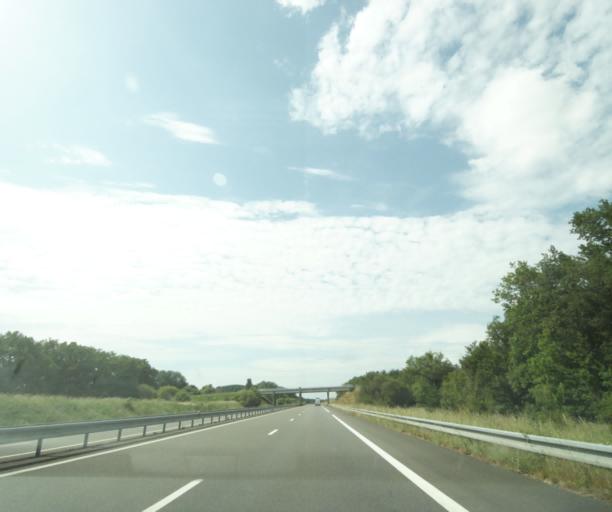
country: FR
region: Pays de la Loire
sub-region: Departement de Maine-et-Loire
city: Baune
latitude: 47.4995
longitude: -0.2810
